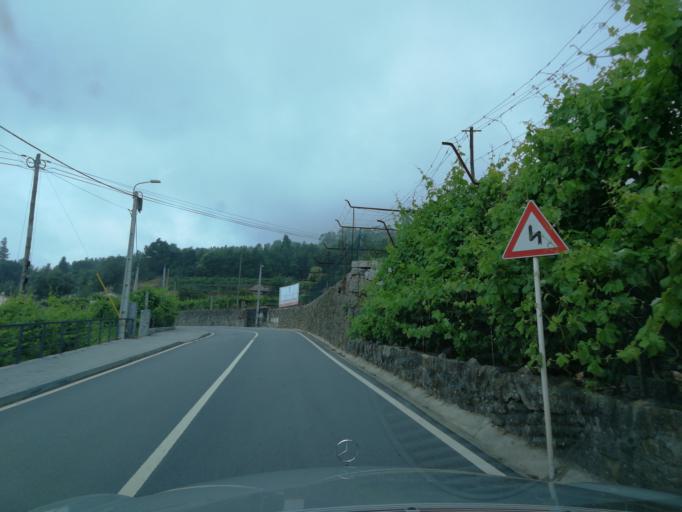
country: PT
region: Braga
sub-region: Braga
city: Braga
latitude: 41.5208
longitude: -8.3674
